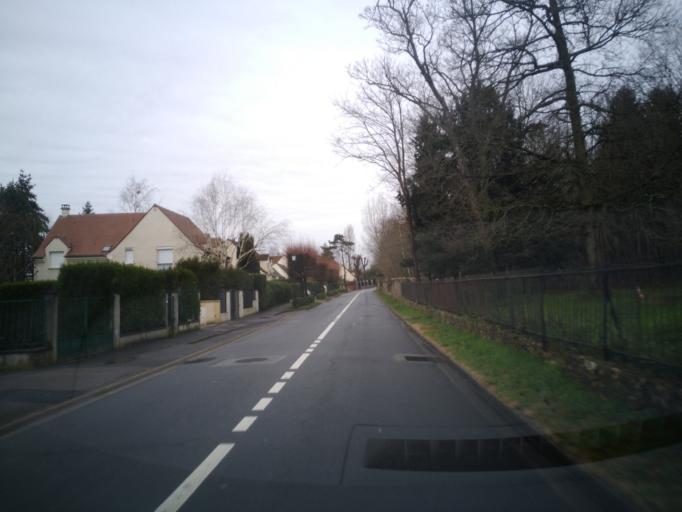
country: FR
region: Ile-de-France
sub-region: Departement des Yvelines
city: Saint-Nom-la-Breteche
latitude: 48.8654
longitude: 2.0236
